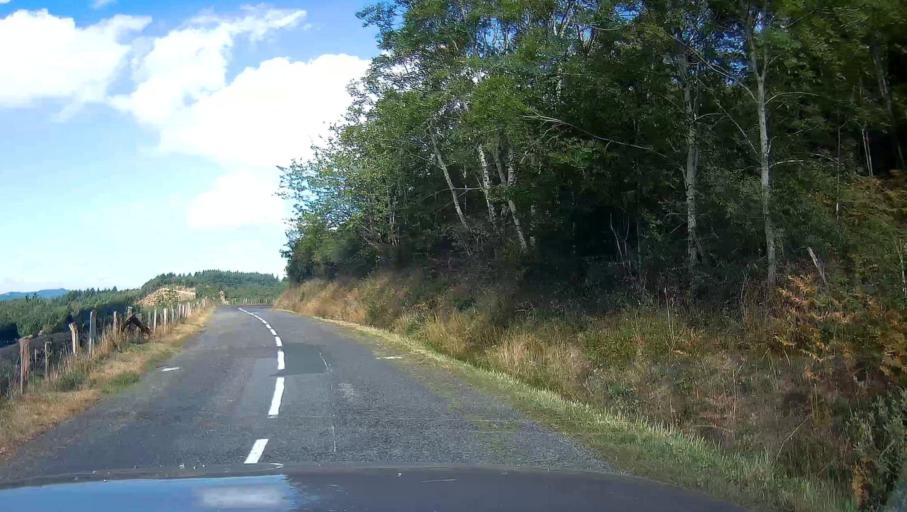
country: FR
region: Rhone-Alpes
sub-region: Departement du Rhone
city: Cogny
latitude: 45.9948
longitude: 4.5575
